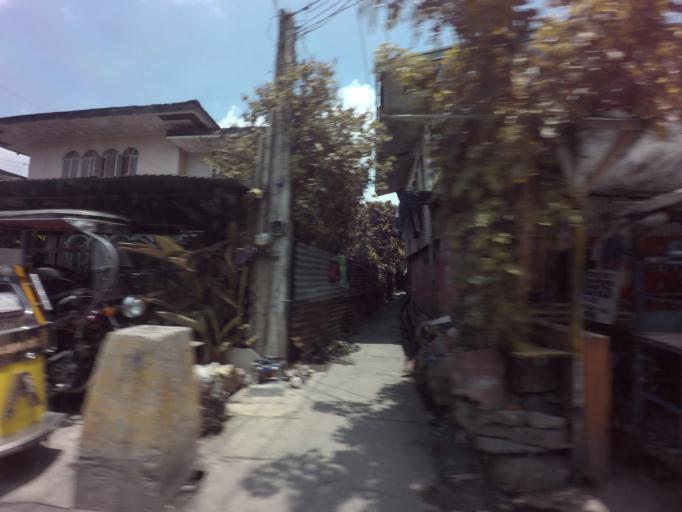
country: PH
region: Calabarzon
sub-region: Province of Laguna
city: San Pedro
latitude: 14.3899
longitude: 121.0499
